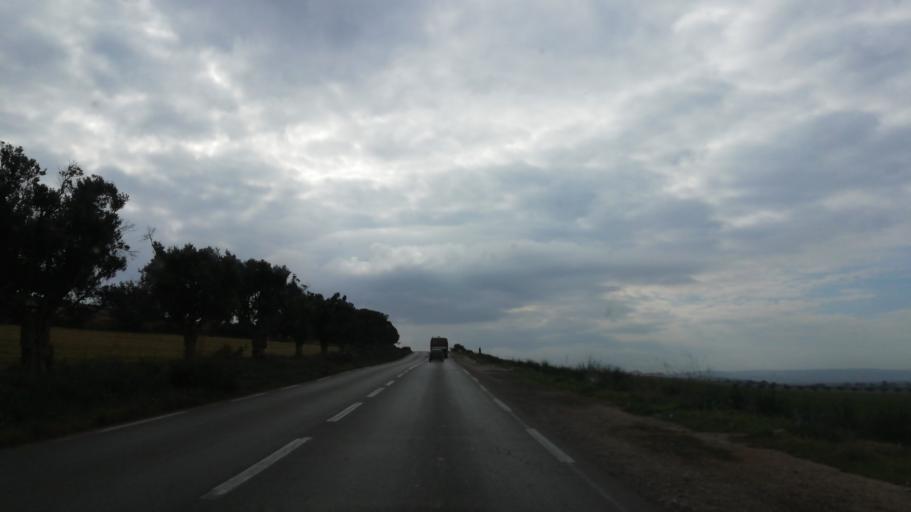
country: DZ
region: Oran
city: Ain el Bya
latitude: 35.7372
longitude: -0.3552
